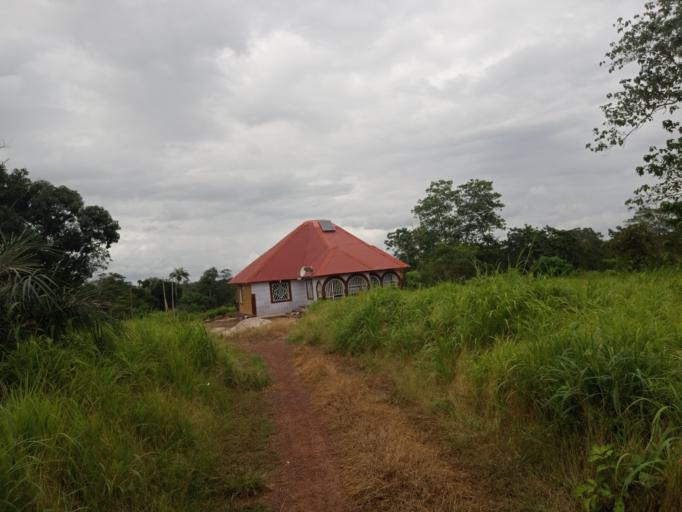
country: SL
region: Northern Province
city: Kamakwie
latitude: 9.4994
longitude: -12.2516
